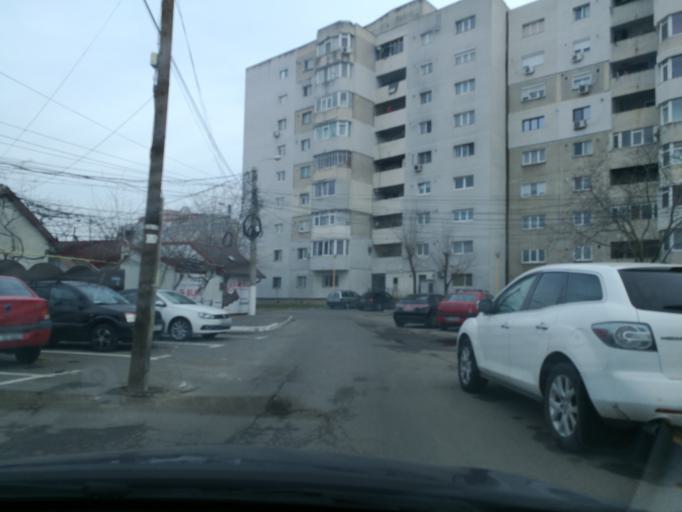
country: RO
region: Constanta
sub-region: Municipiul Constanta
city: Constanta
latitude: 44.1719
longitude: 28.6089
